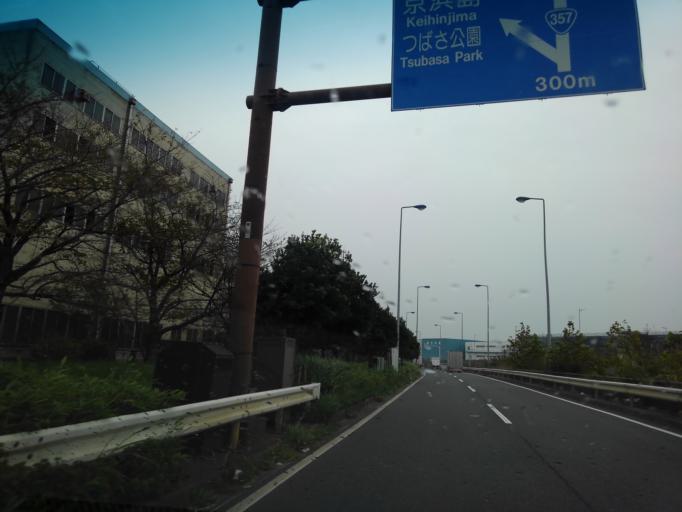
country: JP
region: Kanagawa
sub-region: Kawasaki-shi
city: Kawasaki
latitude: 35.5707
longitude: 139.7601
